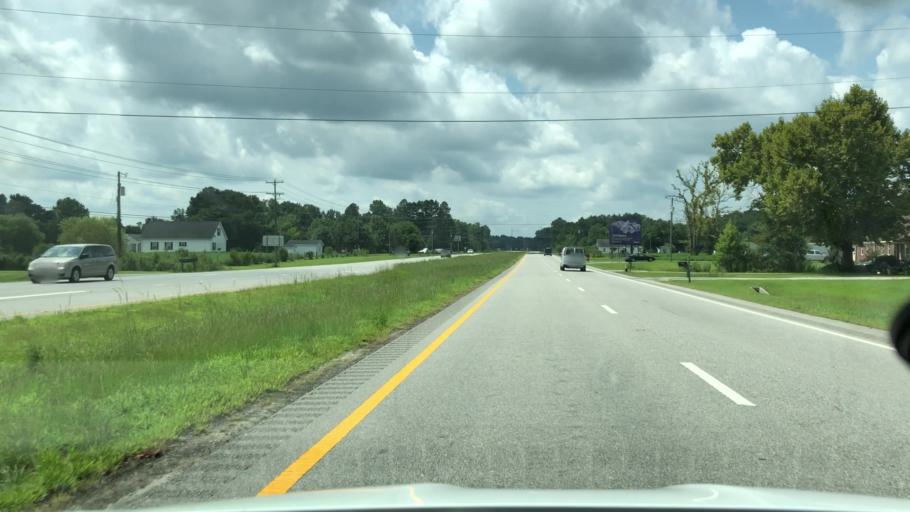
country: US
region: North Carolina
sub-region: Beaufort County
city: Washington
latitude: 35.4831
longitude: -77.1123
